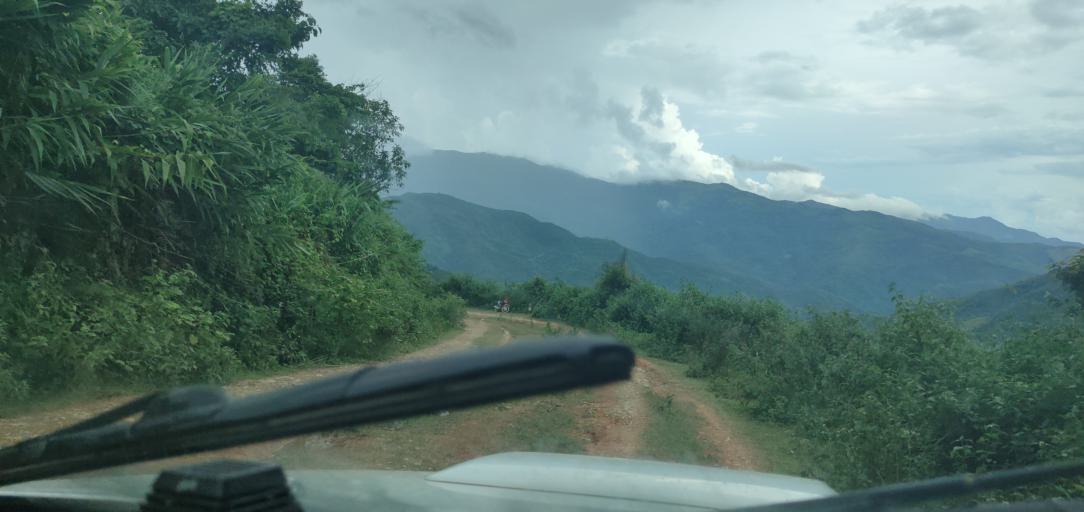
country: LA
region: Phongsali
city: Phongsali
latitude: 21.4415
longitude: 102.3215
